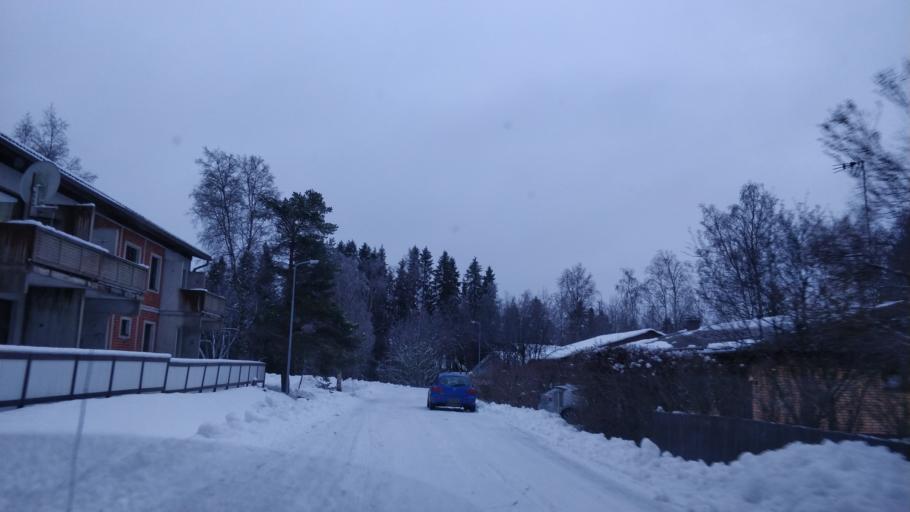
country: FI
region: Lapland
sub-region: Kemi-Tornio
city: Kemi
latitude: 65.7421
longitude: 24.5989
